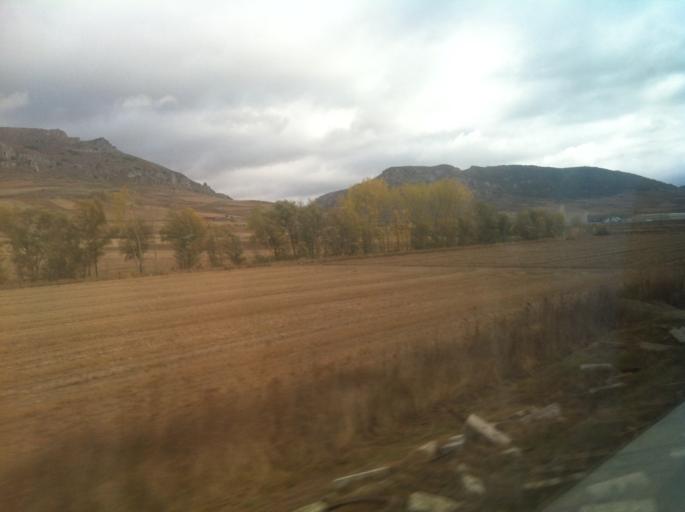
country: ES
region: Castille and Leon
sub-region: Provincia de Burgos
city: Pancorbo
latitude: 42.6255
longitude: -3.1389
